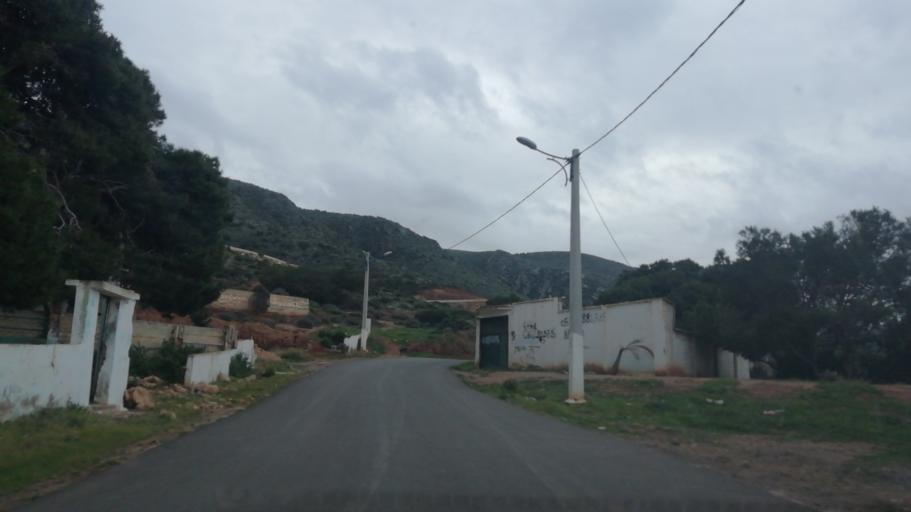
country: DZ
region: Oran
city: Bir el Djir
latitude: 35.7758
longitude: -0.5149
